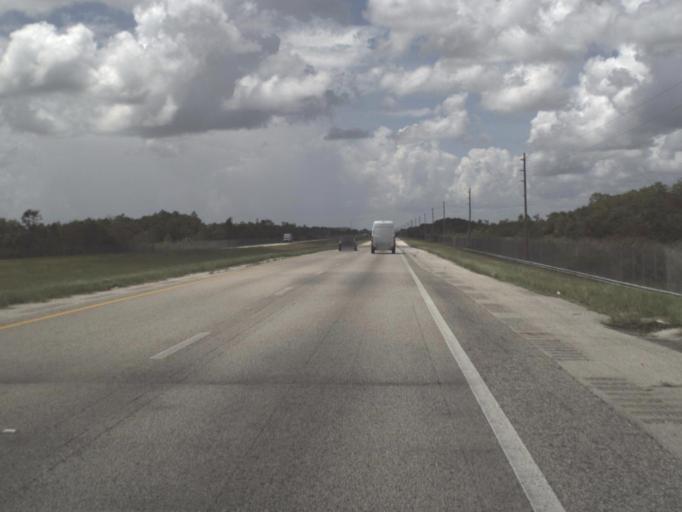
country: US
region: Florida
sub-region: Collier County
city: Immokalee
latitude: 26.1716
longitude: -80.9407
